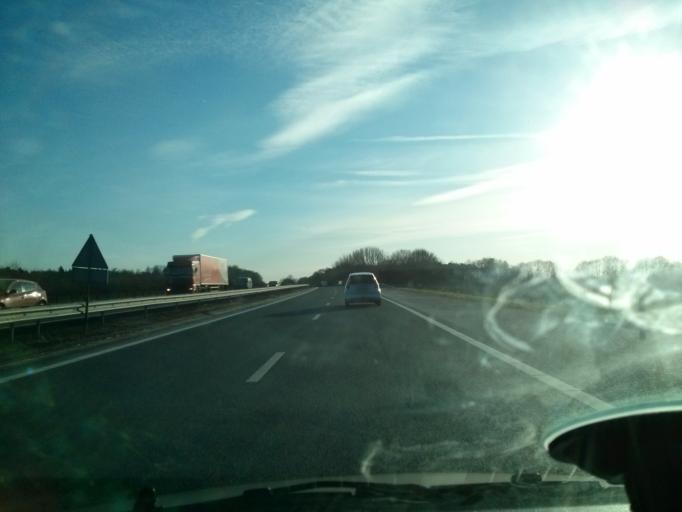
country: NL
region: Gelderland
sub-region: Gemeente Wijchen
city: Bergharen
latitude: 51.8372
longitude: 5.6885
